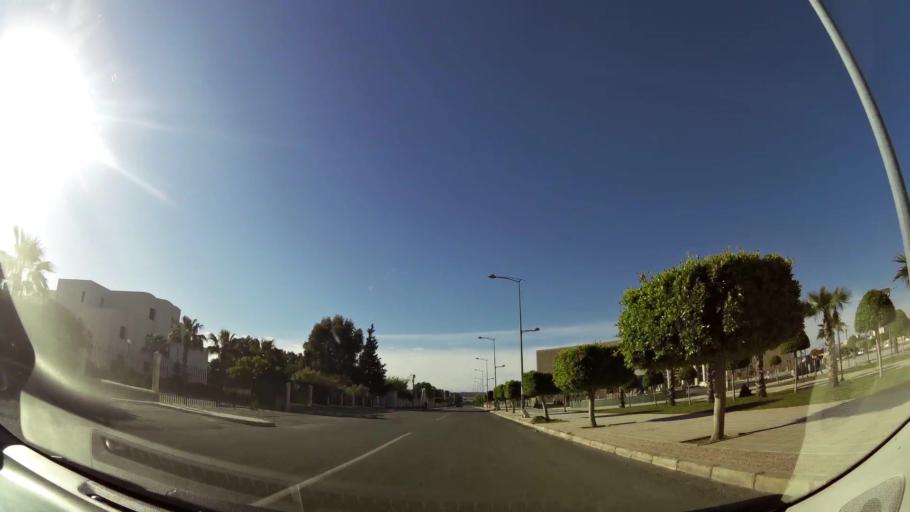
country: MA
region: Oriental
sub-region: Oujda-Angad
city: Oujda
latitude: 34.6616
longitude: -1.9113
